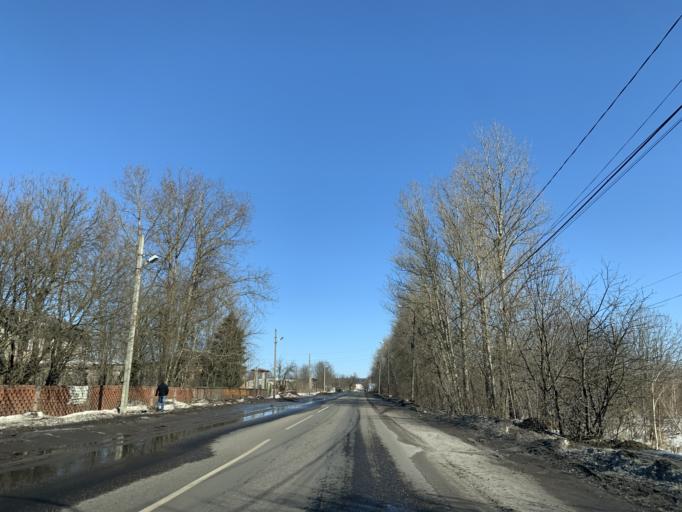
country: RU
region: Jaroslavl
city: Konstantinovskiy
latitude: 57.8386
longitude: 39.5677
